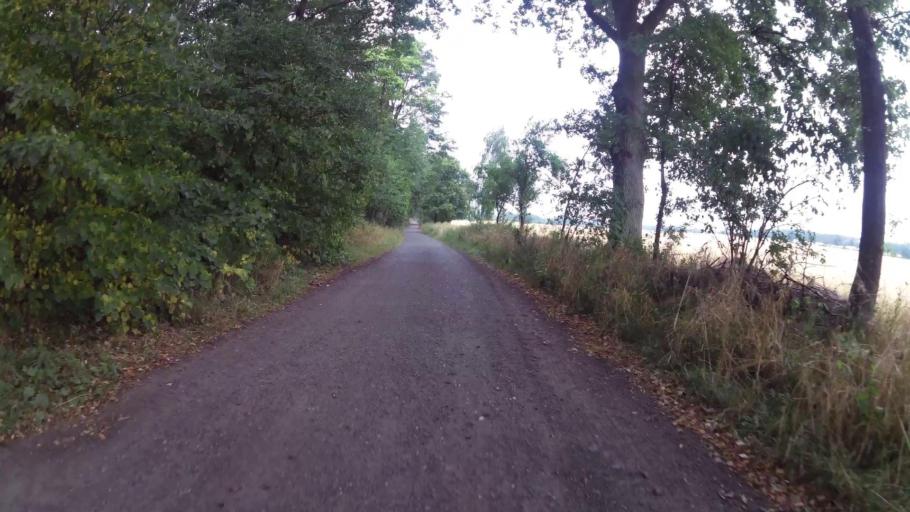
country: PL
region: West Pomeranian Voivodeship
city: Trzcinsko Zdroj
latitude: 52.9006
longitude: 14.6799
